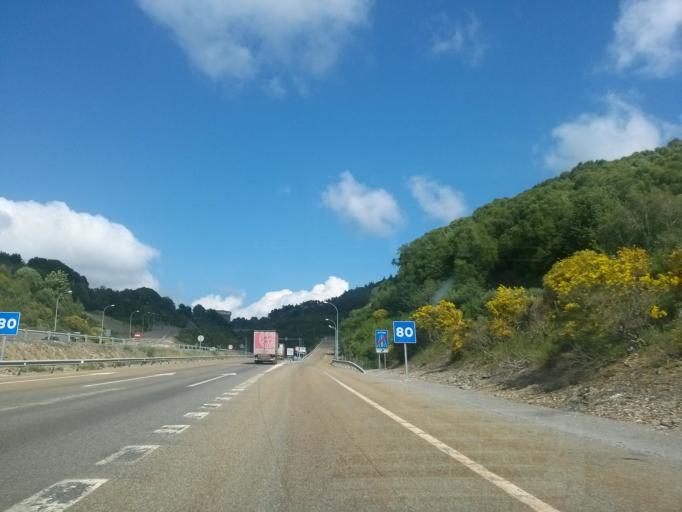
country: ES
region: Castille and Leon
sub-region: Provincia de Leon
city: Balboa
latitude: 42.7269
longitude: -7.0341
